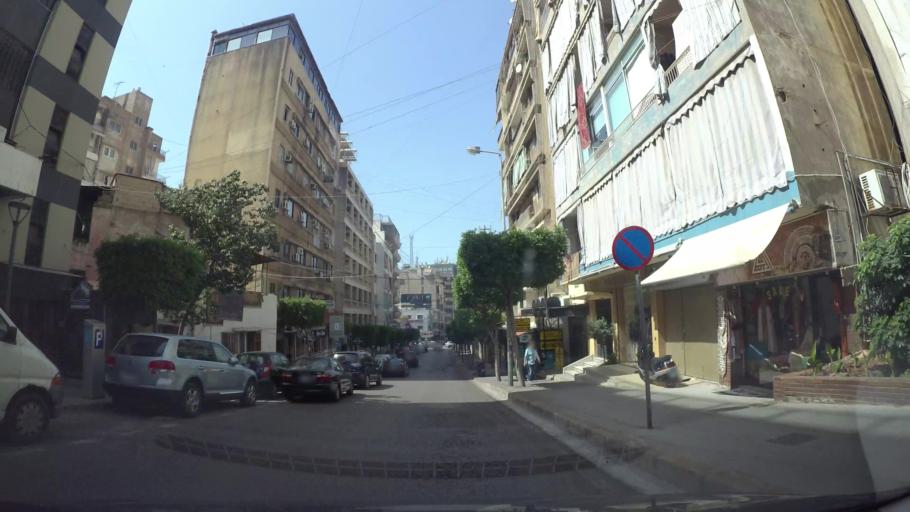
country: LB
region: Beyrouth
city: Ra's Bayrut
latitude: 33.8927
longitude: 35.4833
